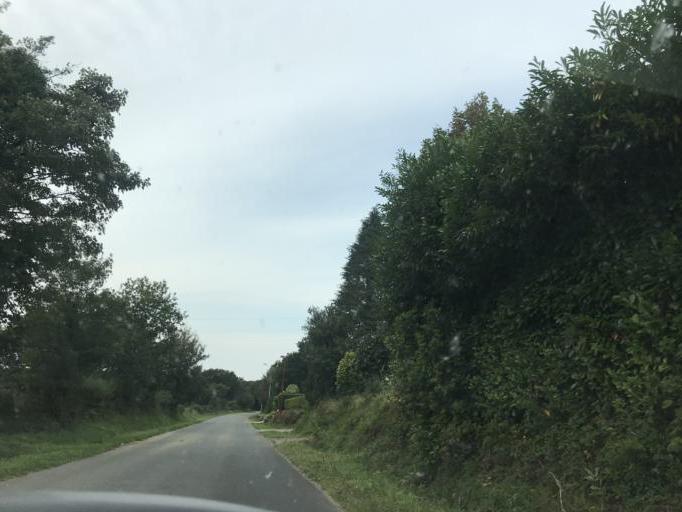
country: FR
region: Brittany
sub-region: Departement du Finistere
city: Plouneour-Menez
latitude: 48.3635
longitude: -3.8519
